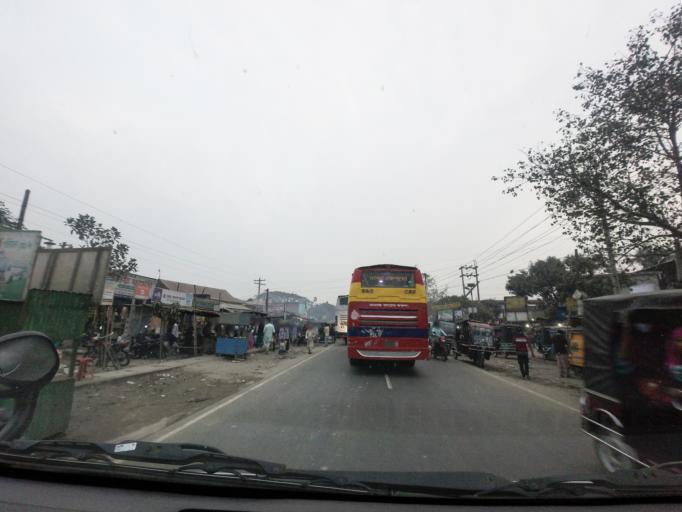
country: BD
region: Dhaka
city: Bajitpur
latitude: 24.2097
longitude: 90.8551
